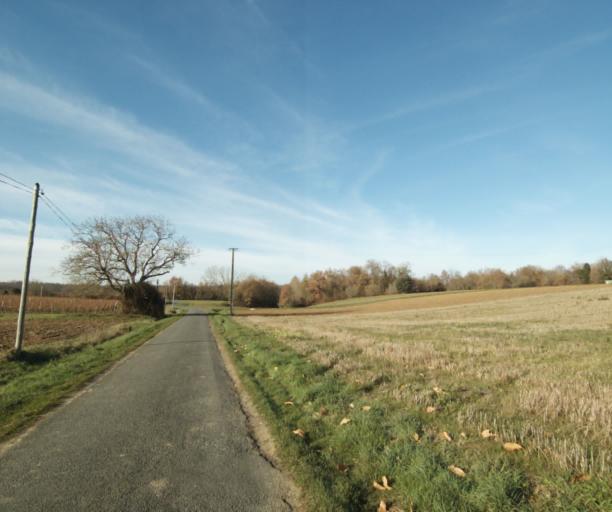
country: FR
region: Poitou-Charentes
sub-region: Departement de la Charente-Maritime
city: Burie
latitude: 45.7852
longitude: -0.4377
